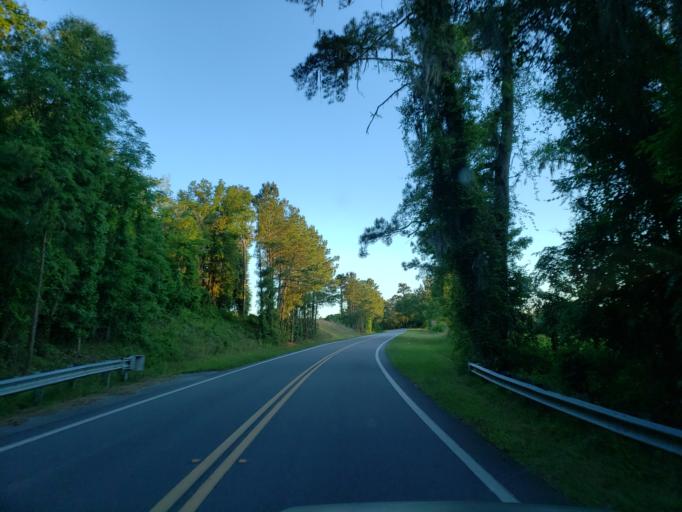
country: US
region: Florida
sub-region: Madison County
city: Madison
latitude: 30.6072
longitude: -83.2542
